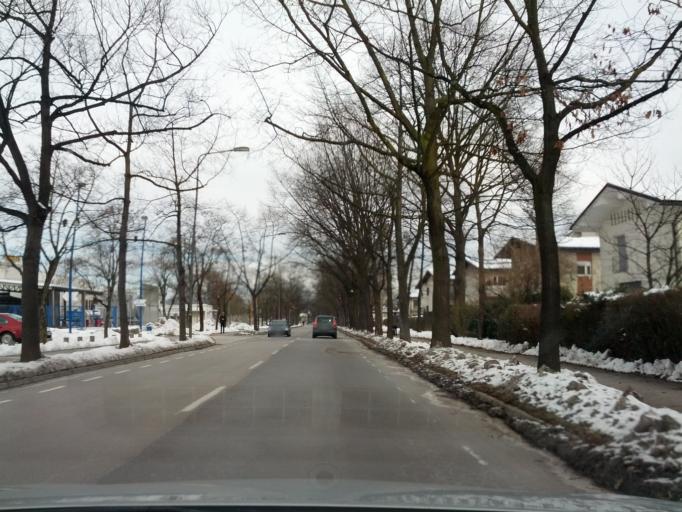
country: SI
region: Ljubljana
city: Ljubljana
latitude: 46.0791
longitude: 14.5066
